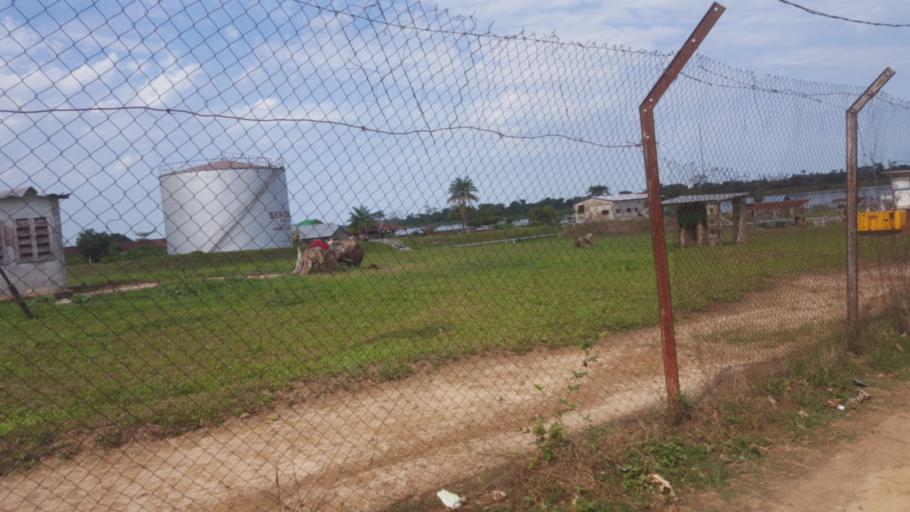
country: CD
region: Bandundu
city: Bandundu
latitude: -3.3013
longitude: 17.3697
